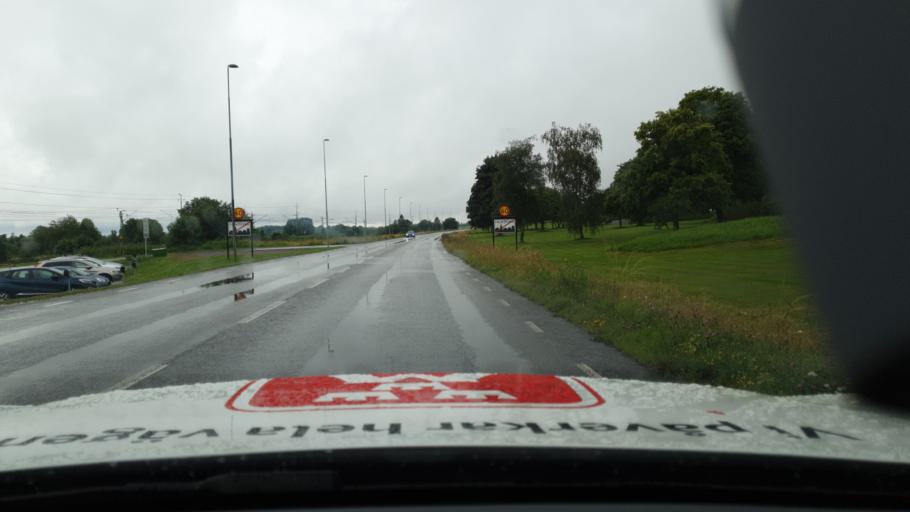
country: SE
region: Vaestra Goetaland
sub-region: Falkopings Kommun
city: Falkoeping
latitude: 58.1665
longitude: 13.5326
